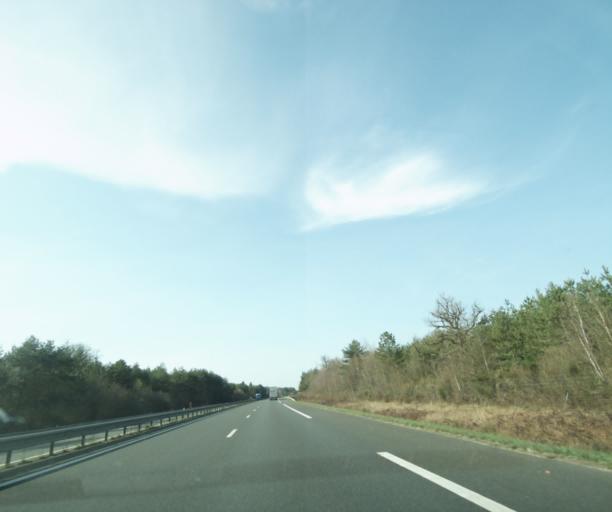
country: FR
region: Centre
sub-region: Departement du Loir-et-Cher
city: Lamotte-Beuvron
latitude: 47.6020
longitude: 1.9752
